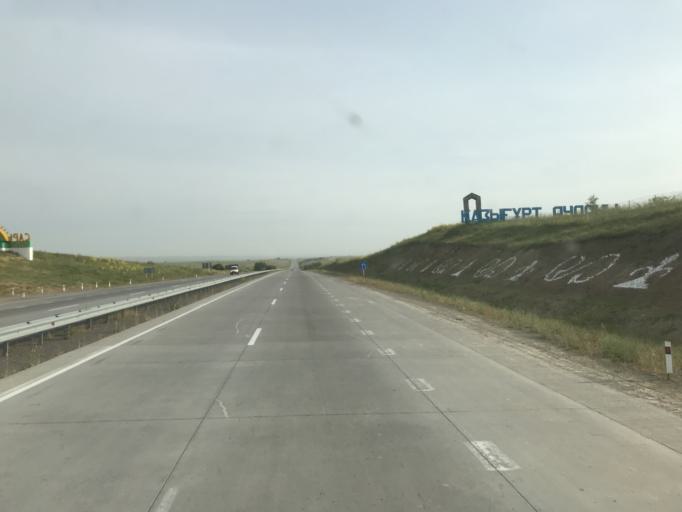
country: KZ
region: Ongtustik Qazaqstan
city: Qazyqurt
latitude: 41.6065
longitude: 69.4043
